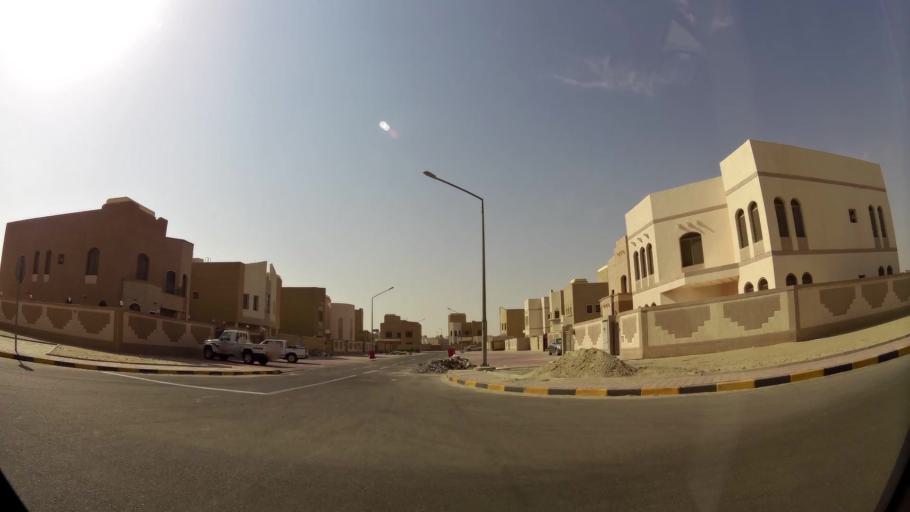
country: KW
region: Al Ahmadi
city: Al Wafrah
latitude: 28.7961
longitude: 48.0721
